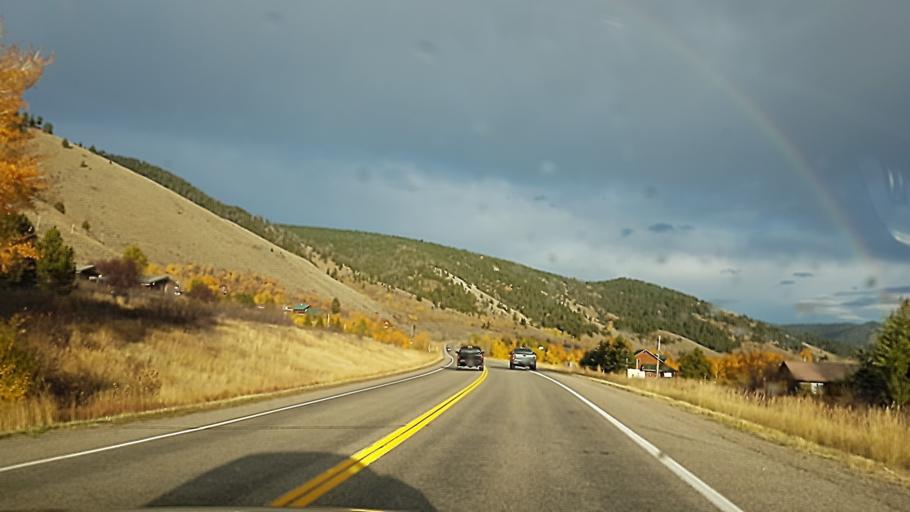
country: US
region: Montana
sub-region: Gallatin County
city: West Yellowstone
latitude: 44.6626
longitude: -111.3785
